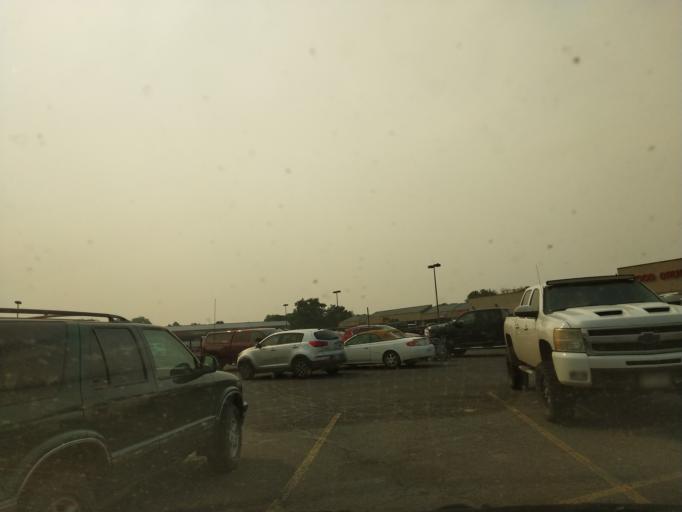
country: US
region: Colorado
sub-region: Mesa County
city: Clifton
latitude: 39.0867
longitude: -108.4611
